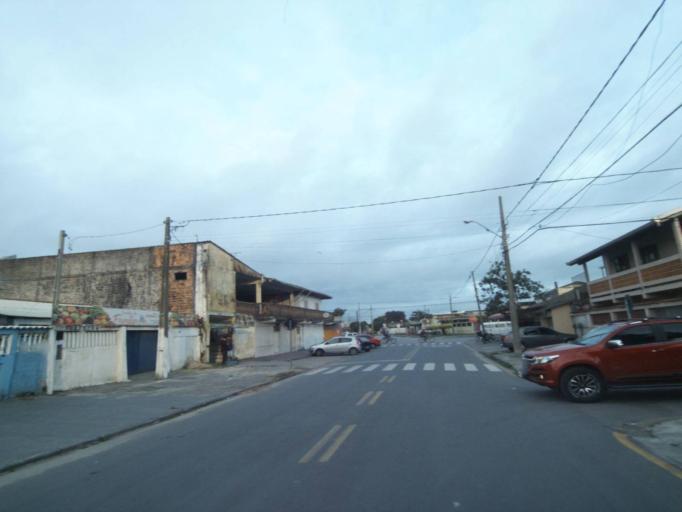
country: BR
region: Parana
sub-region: Paranagua
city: Paranagua
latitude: -25.5182
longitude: -48.5424
